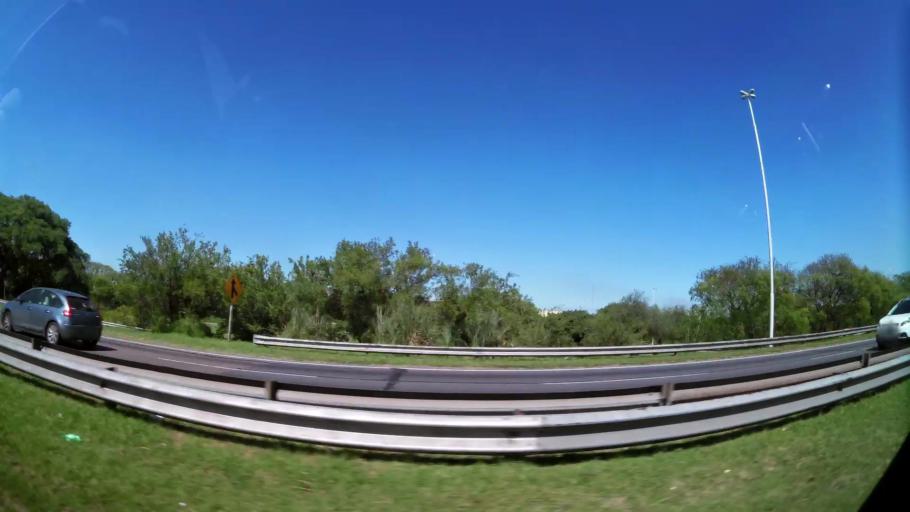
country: AR
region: Buenos Aires
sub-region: Partido de Tigre
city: Tigre
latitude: -34.4718
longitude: -58.5666
